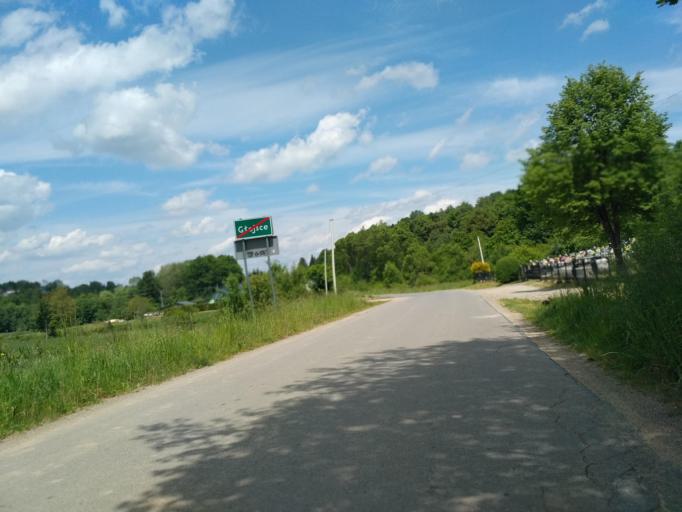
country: PL
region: Subcarpathian Voivodeship
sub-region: Powiat krosnienski
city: Dukla
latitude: 49.5822
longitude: 21.6240
